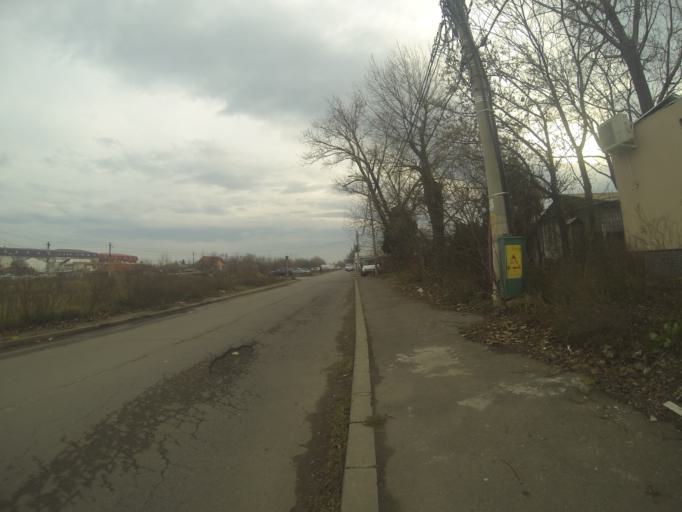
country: RO
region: Ilfov
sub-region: Comuna Jilava
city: Jilava
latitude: 44.3755
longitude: 26.0866
